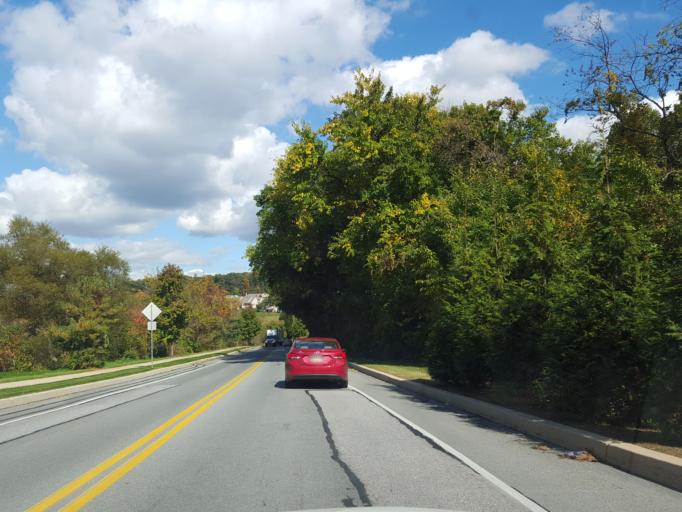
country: US
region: Pennsylvania
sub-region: York County
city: Spry
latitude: 39.9410
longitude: -76.6638
